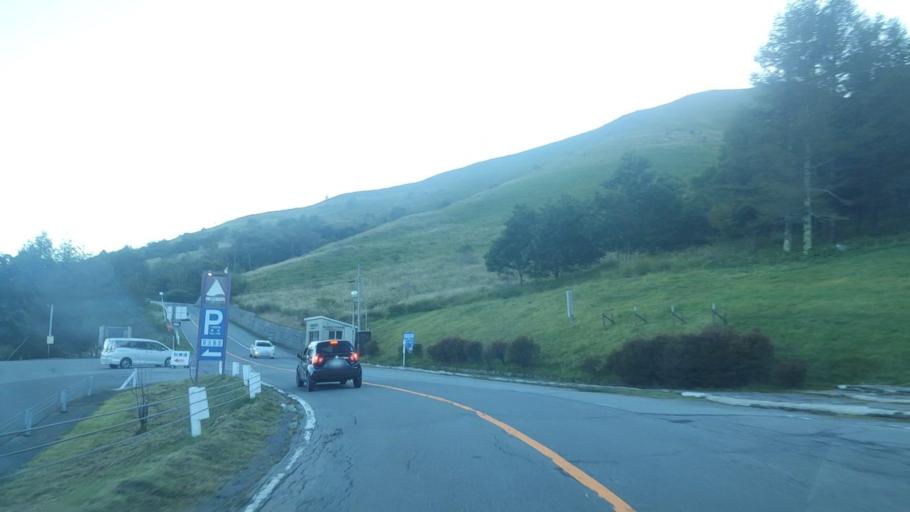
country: JP
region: Nagano
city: Suwa
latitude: 36.1013
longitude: 138.2116
